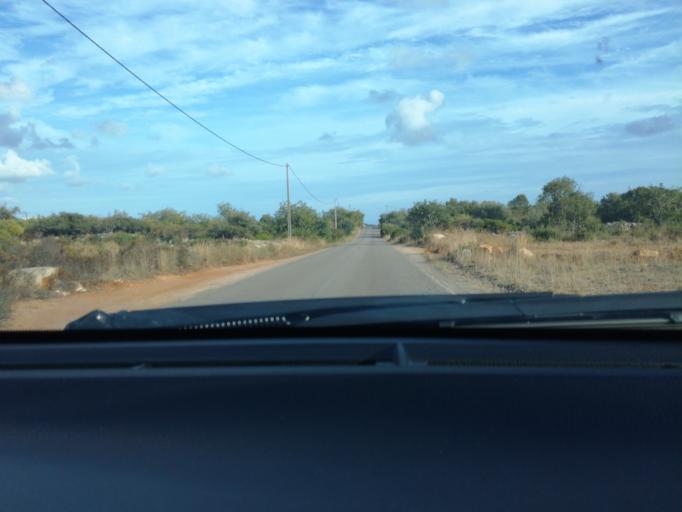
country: PT
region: Faro
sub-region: Olhao
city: Laranjeiro
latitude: 37.0794
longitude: -7.8302
